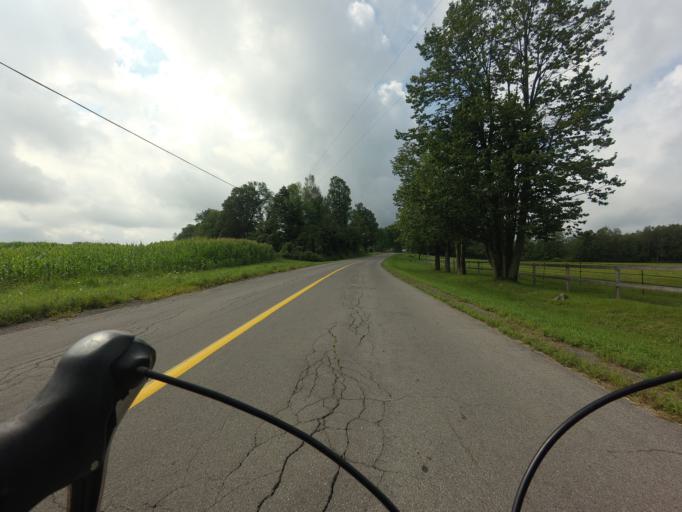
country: CA
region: Ontario
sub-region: Lanark County
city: Smiths Falls
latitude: 44.9663
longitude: -75.8087
